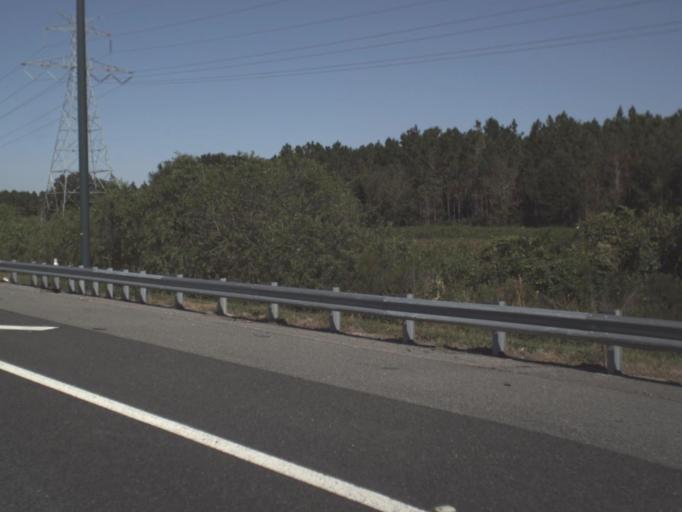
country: US
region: Florida
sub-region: Lake County
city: Hawthorne
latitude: 28.7567
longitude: -81.9399
